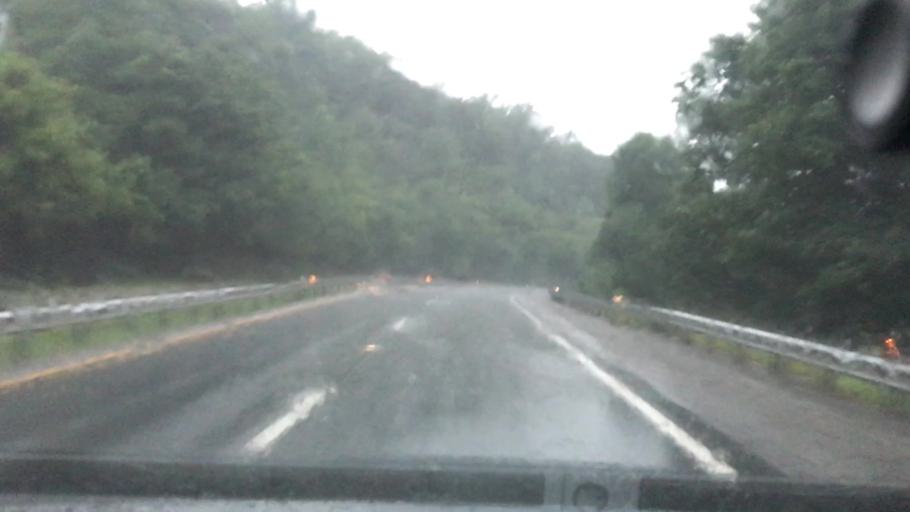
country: US
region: Virginia
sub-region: Giles County
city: Pearisburg
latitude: 37.3471
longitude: -80.7603
